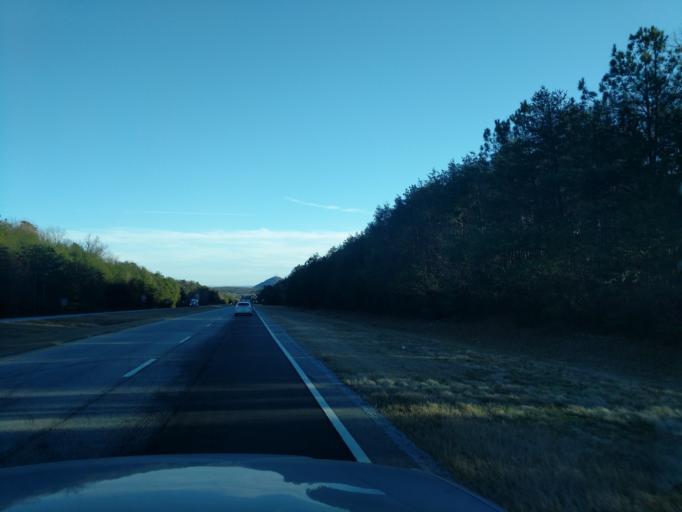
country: US
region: Georgia
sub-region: Stephens County
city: Toccoa
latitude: 34.5856
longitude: -83.4125
